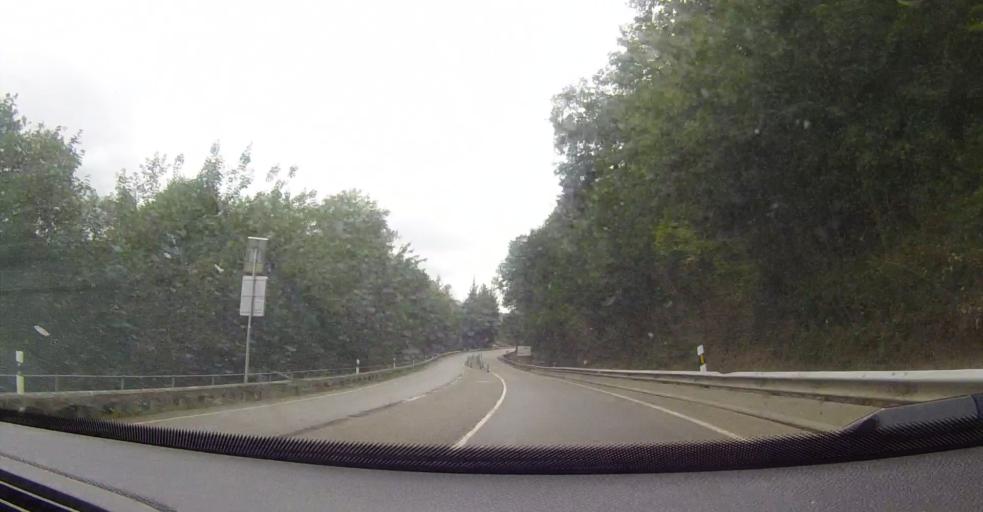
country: ES
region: Asturias
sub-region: Province of Asturias
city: Nava
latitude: 43.3566
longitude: -5.4550
